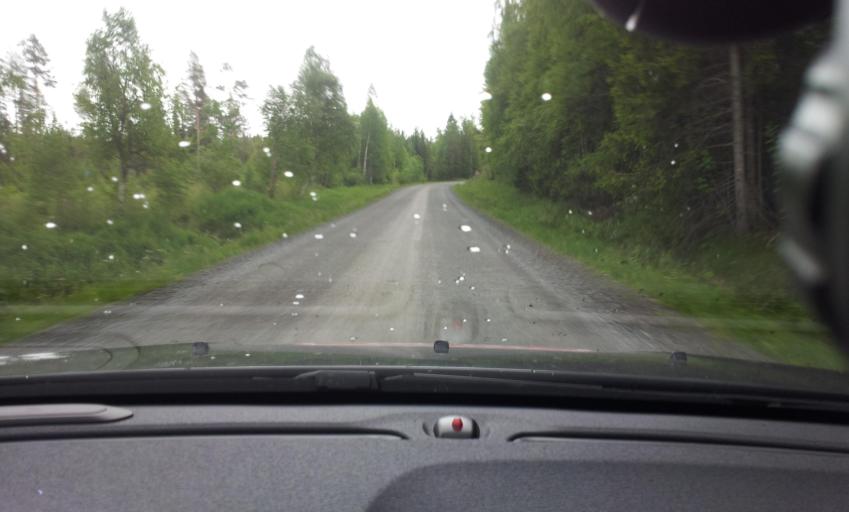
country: SE
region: Jaemtland
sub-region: OEstersunds Kommun
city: Brunflo
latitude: 63.1244
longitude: 15.0898
